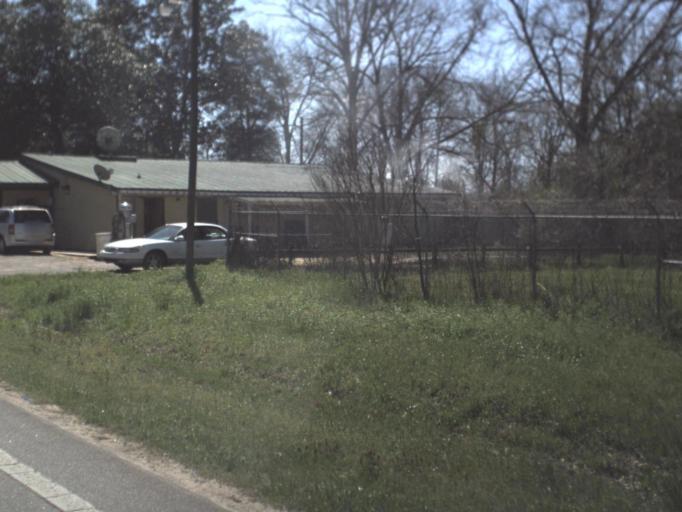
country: US
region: Florida
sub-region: Gadsden County
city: Gretna
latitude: 30.6545
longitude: -84.6036
